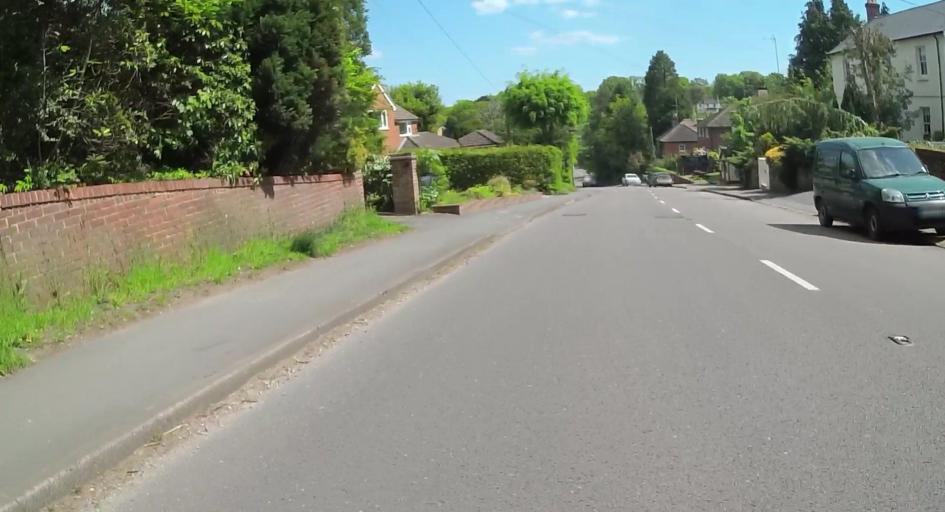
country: GB
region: England
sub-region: Surrey
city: Farnham
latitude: 51.1933
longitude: -0.8134
